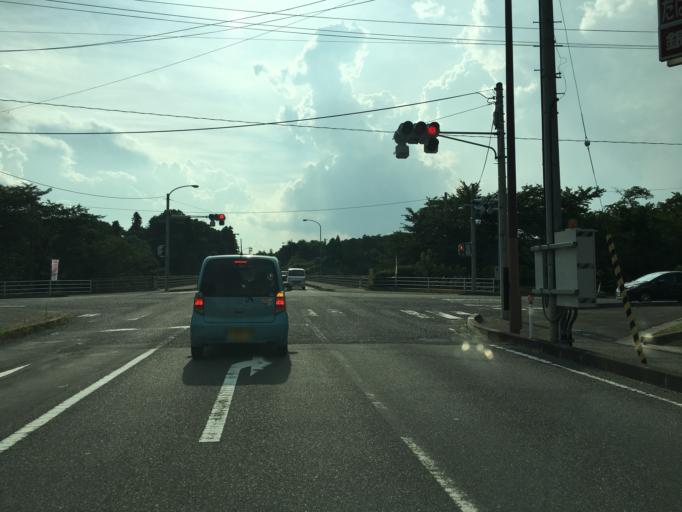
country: JP
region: Fukushima
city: Miharu
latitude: 37.4470
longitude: 140.4278
